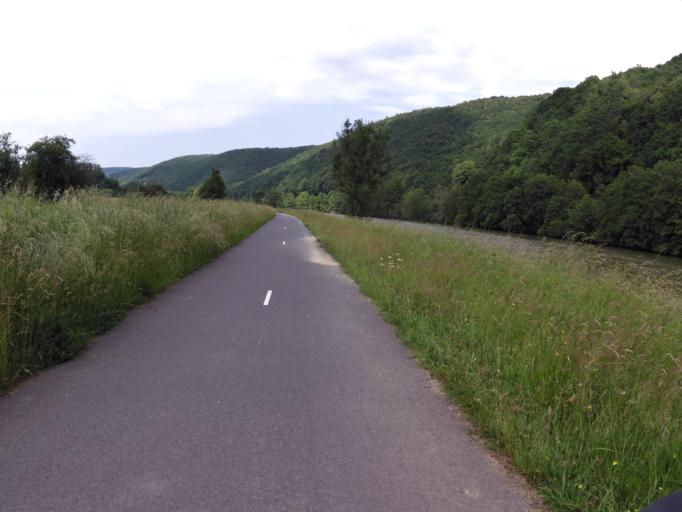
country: FR
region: Champagne-Ardenne
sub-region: Departement des Ardennes
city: Neufmanil
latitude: 49.8394
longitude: 4.7810
